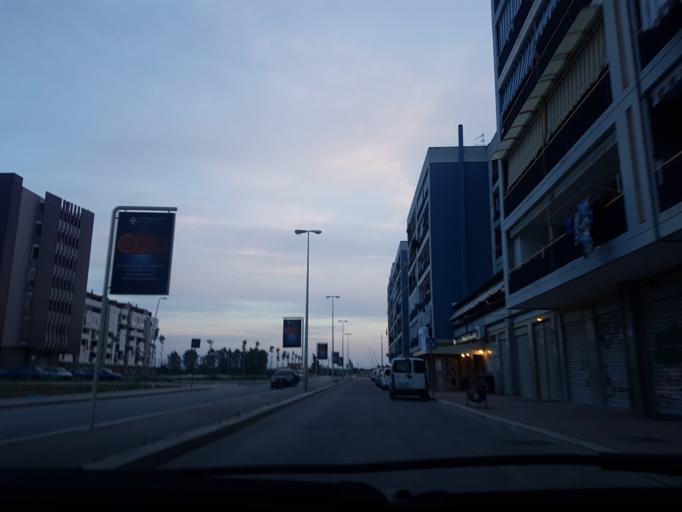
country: IT
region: Apulia
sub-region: Provincia di Barletta - Andria - Trani
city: Barletta
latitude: 41.3066
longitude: 16.2649
